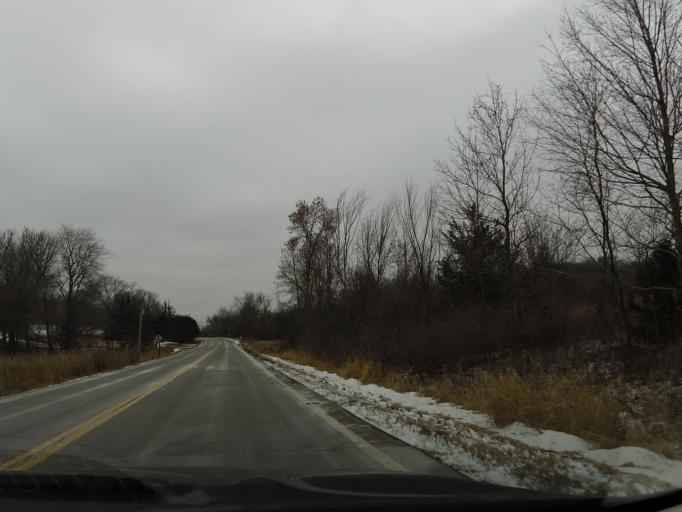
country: US
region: Minnesota
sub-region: Hennepin County
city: Medina
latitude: 45.0114
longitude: -93.6090
